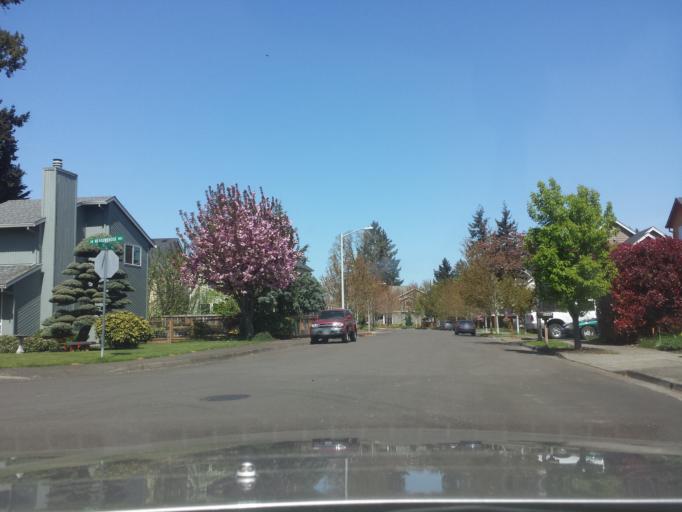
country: US
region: Oregon
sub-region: Washington County
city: Aloha
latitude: 45.4847
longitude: -122.8592
